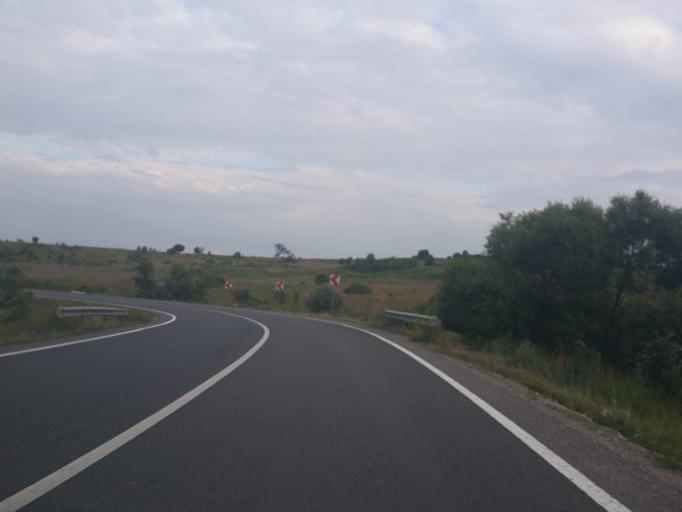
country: RO
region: Cluj
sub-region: Comuna Sanpaul
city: Sanpaul
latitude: 46.9277
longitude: 23.3982
